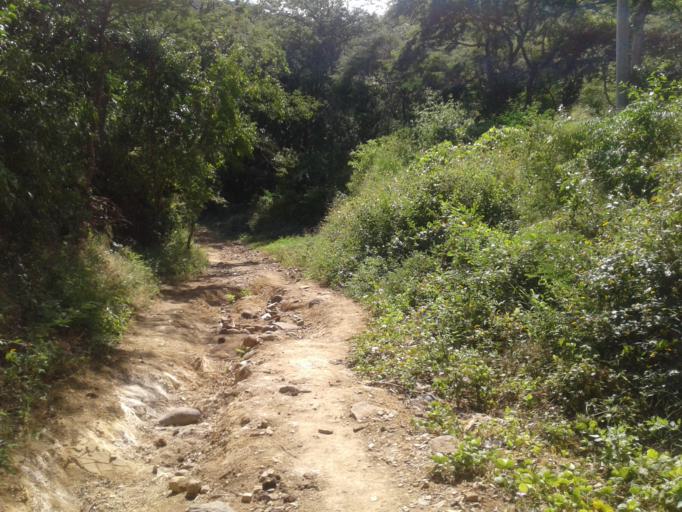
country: NI
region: Carazo
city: Santa Teresa
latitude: 11.6258
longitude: -86.1902
